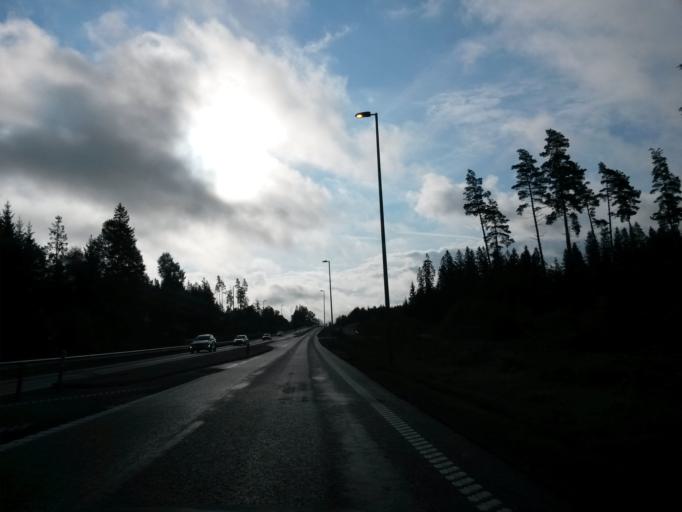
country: SE
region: Vaestra Goetaland
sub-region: Boras Kommun
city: Ganghester
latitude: 57.6749
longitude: 12.9905
